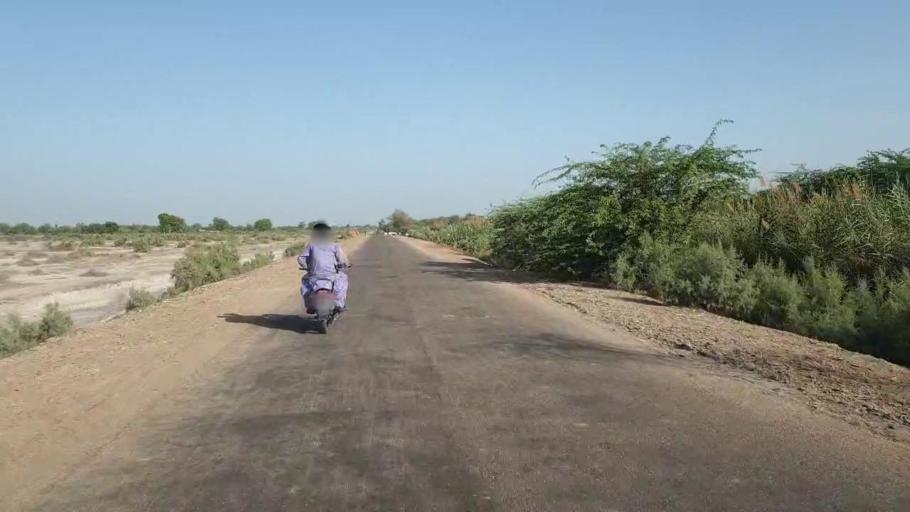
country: PK
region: Sindh
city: Nawabshah
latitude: 26.3891
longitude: 68.4512
